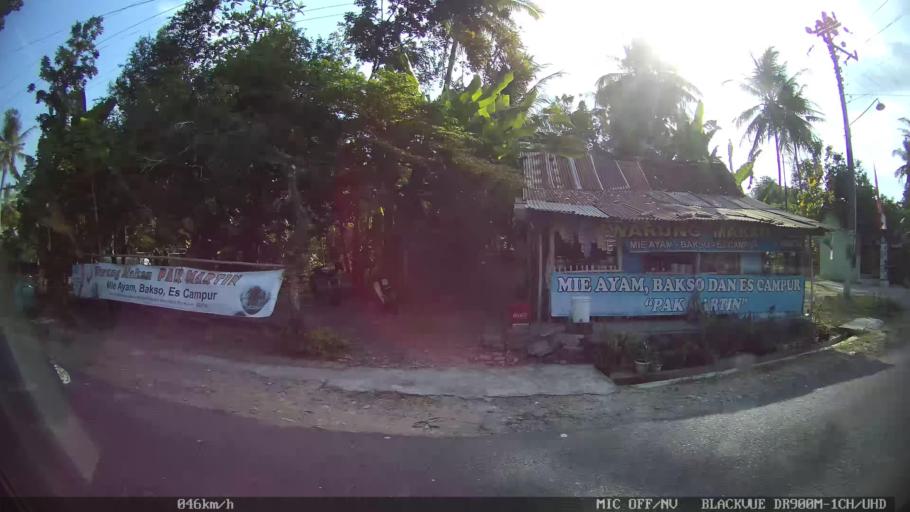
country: ID
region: Daerah Istimewa Yogyakarta
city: Kasihan
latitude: -7.8544
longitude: 110.3193
